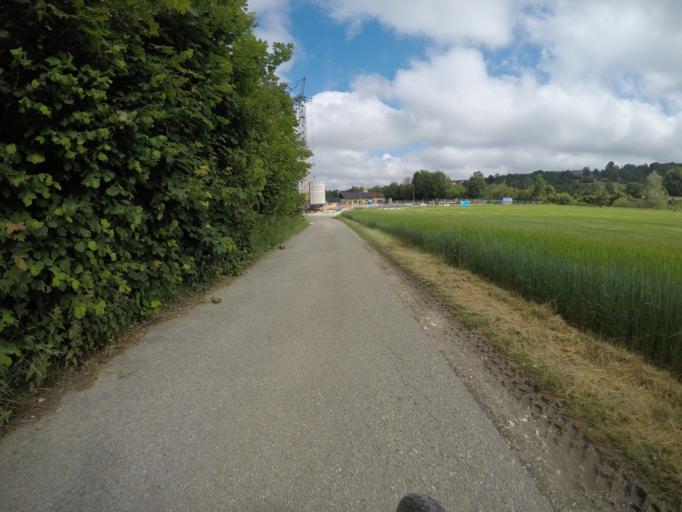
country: DE
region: Baden-Wuerttemberg
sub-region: Tuebingen Region
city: Lonsee
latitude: 48.5292
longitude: 9.9307
